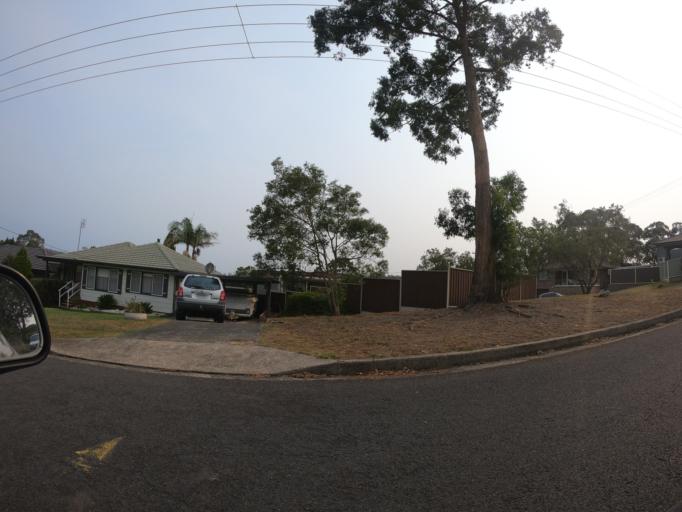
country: AU
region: New South Wales
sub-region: Wollongong
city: Cordeaux Heights
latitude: -34.4525
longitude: 150.8327
